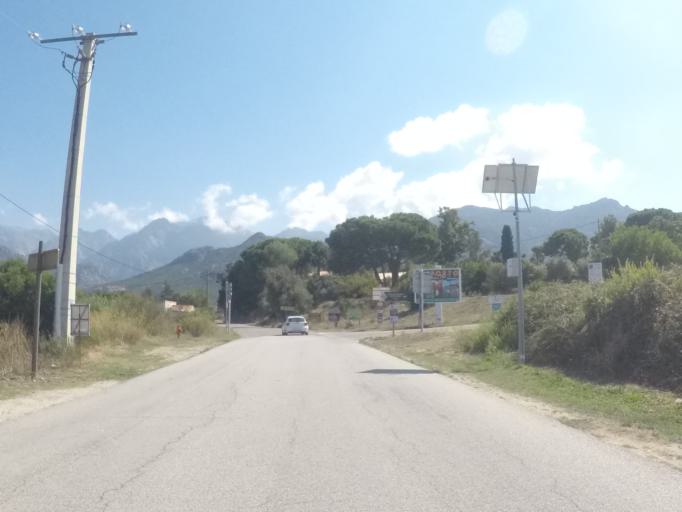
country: FR
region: Corsica
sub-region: Departement de la Haute-Corse
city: Calenzana
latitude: 42.4904
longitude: 8.7972
